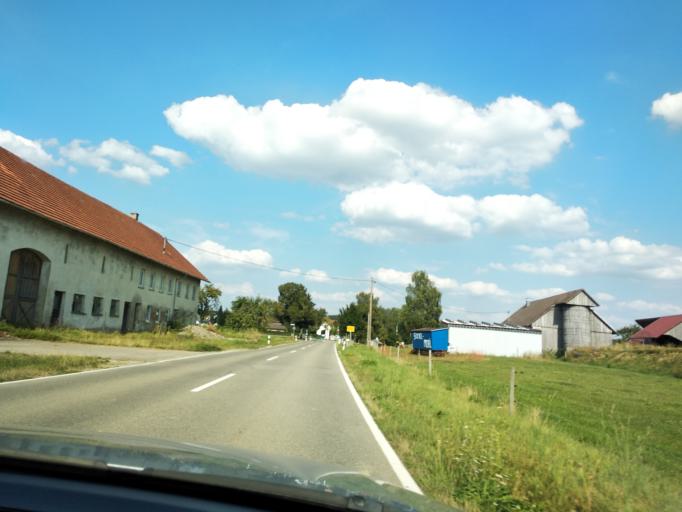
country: DE
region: Bavaria
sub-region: Swabia
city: Ungerhausen
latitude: 48.0030
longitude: 10.2597
